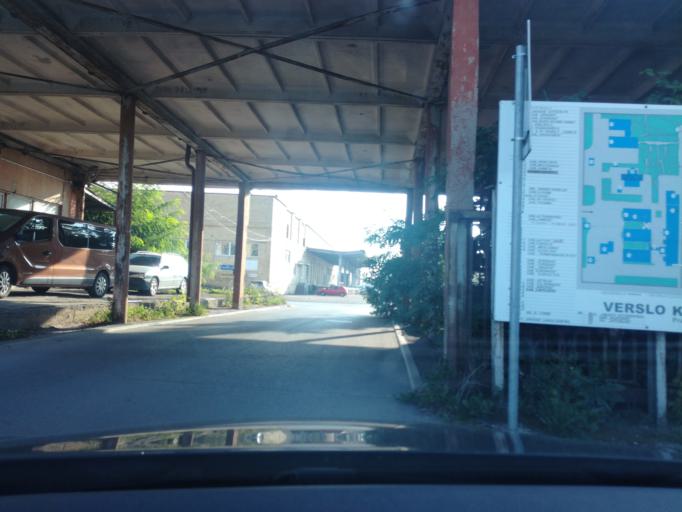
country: LT
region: Alytaus apskritis
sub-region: Alytus
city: Alytus
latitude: 54.4334
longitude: 24.0197
